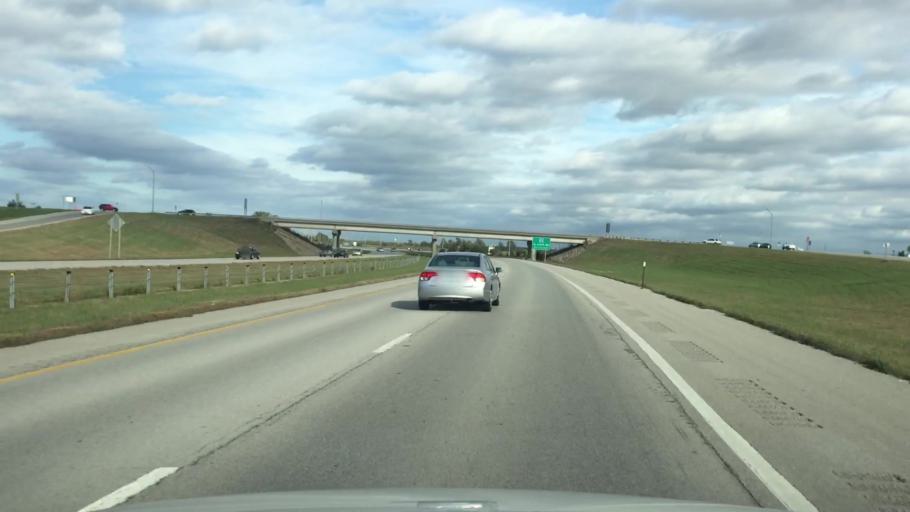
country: US
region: Kansas
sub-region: Douglas County
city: Eudora
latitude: 38.9343
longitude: -95.1037
